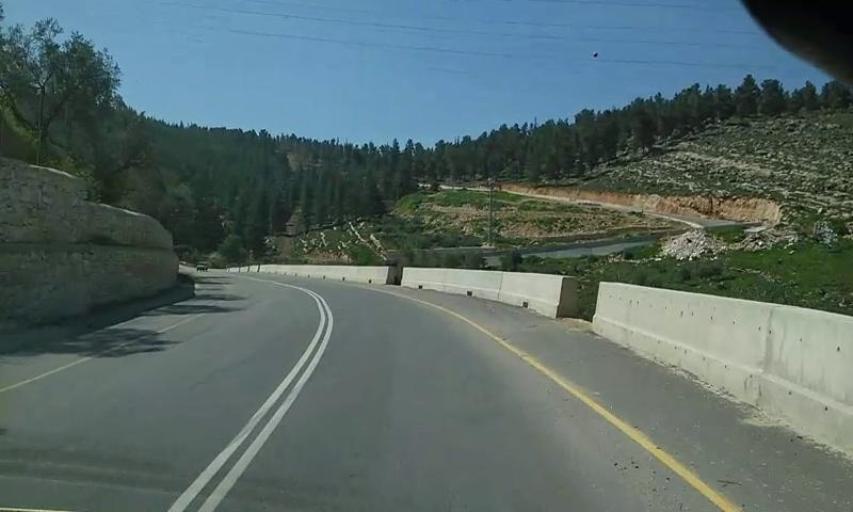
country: PS
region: West Bank
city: Nahhalin
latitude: 31.6788
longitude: 35.1104
